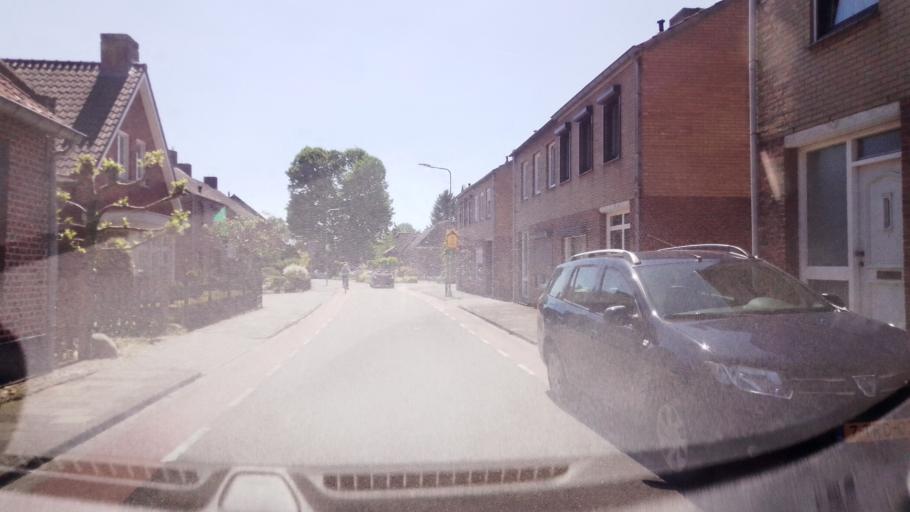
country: NL
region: Limburg
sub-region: Gemeente Venlo
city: Tegelen
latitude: 51.3302
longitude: 6.0952
